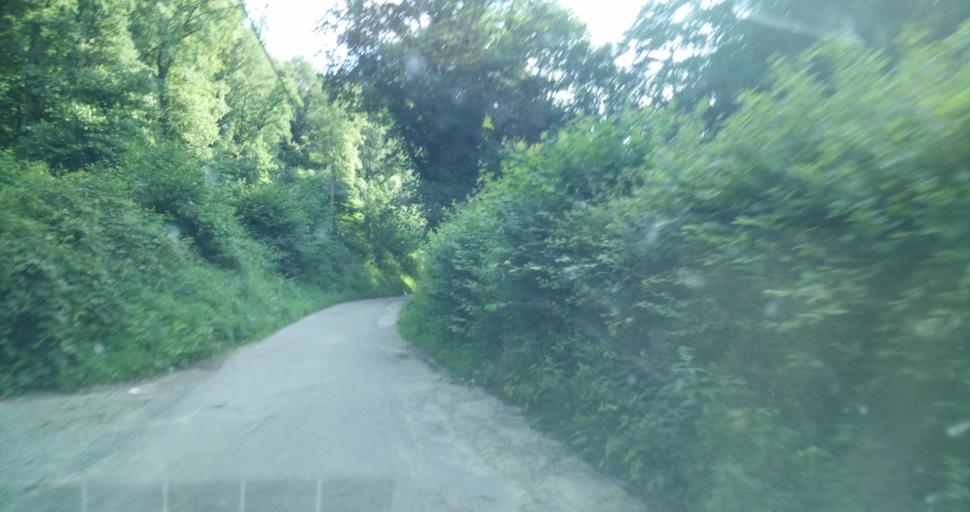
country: BE
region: Wallonia
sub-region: Province du Brabant Wallon
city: Braine-le-Chateau
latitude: 50.6952
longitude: 4.3068
